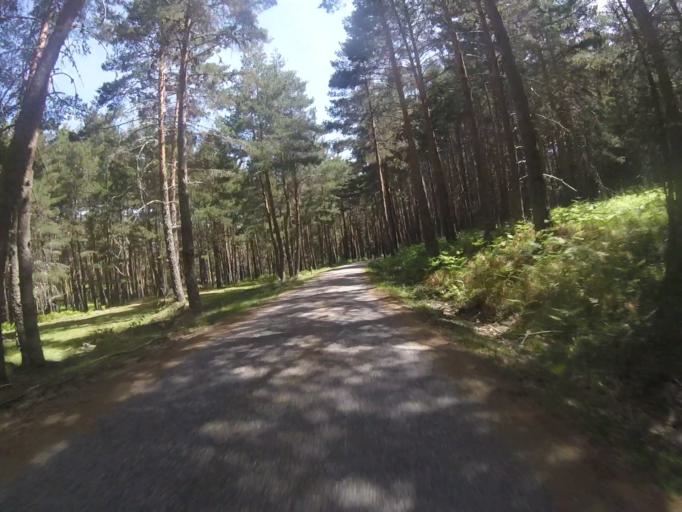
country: ES
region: Madrid
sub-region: Provincia de Madrid
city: Cercedilla
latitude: 40.8123
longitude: -4.0325
